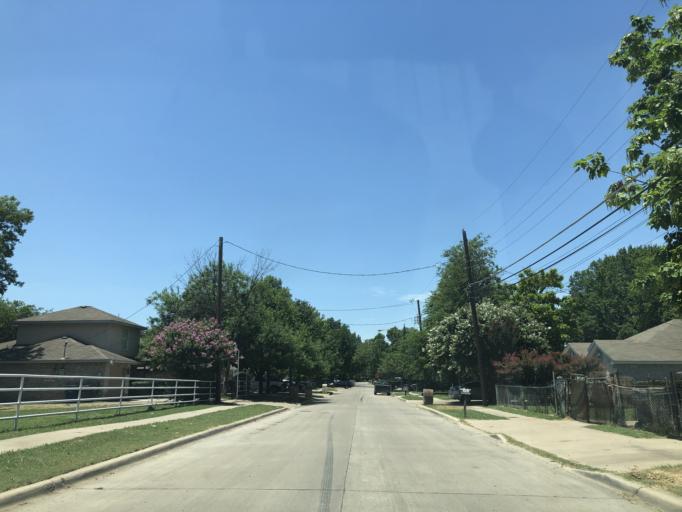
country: US
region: Texas
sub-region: Dallas County
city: Cockrell Hill
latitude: 32.7940
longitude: -96.8937
